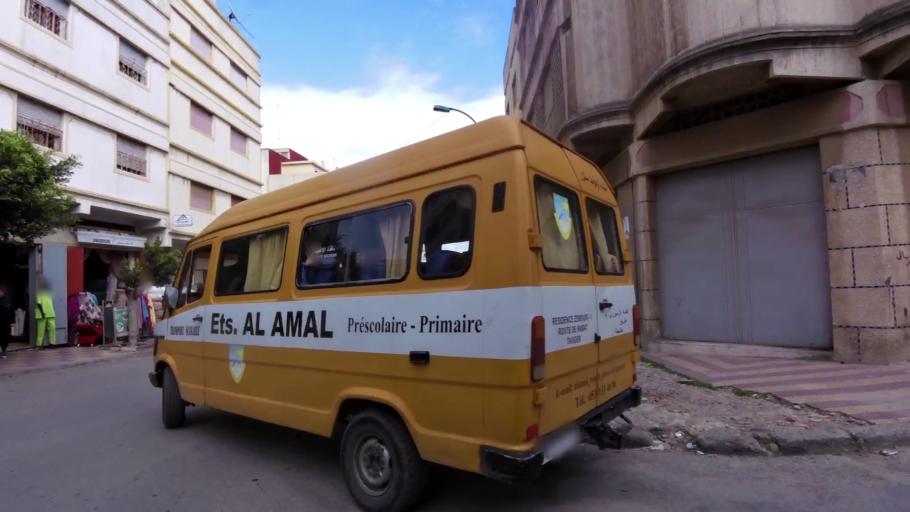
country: MA
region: Tanger-Tetouan
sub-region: Tanger-Assilah
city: Tangier
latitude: 35.7573
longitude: -5.8026
